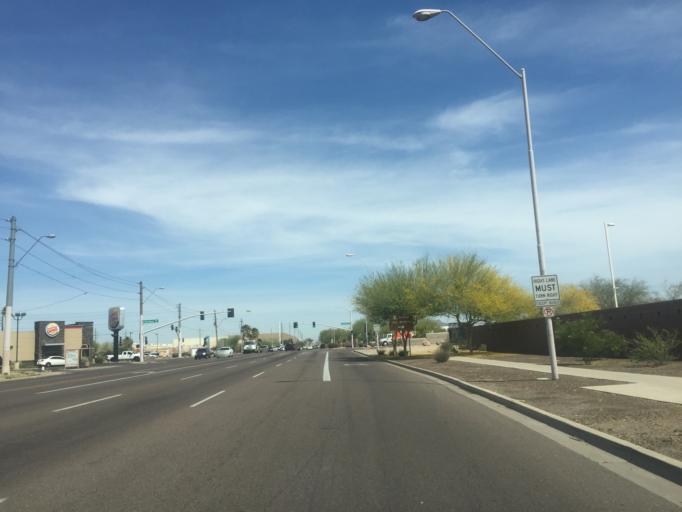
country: US
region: Arizona
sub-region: Maricopa County
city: Phoenix
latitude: 33.4356
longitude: -112.0477
